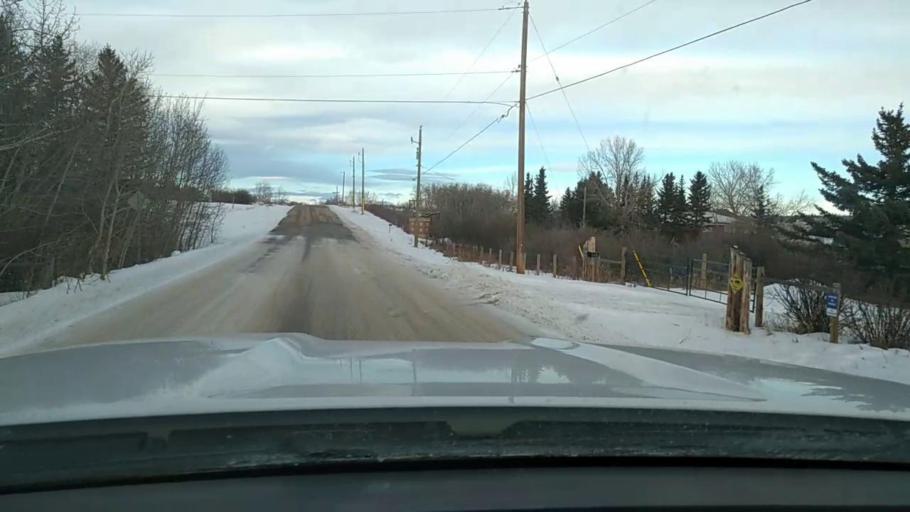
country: CA
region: Alberta
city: Cochrane
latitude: 51.1490
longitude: -114.2663
